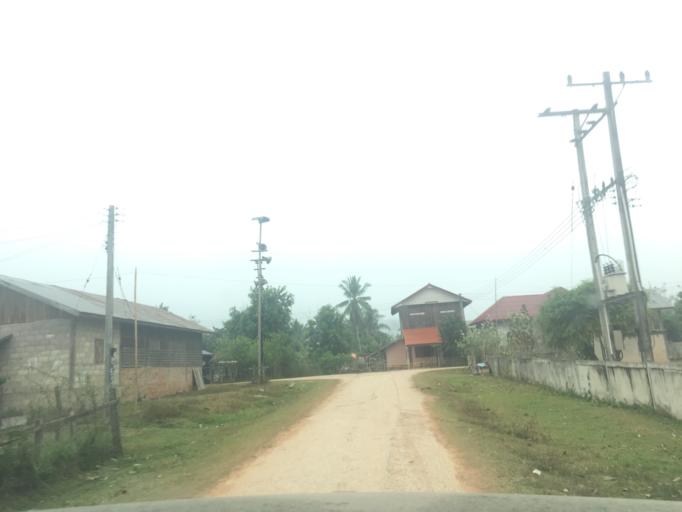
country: LA
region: Xiagnabouli
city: Sainyabuli
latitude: 19.0357
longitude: 101.5247
